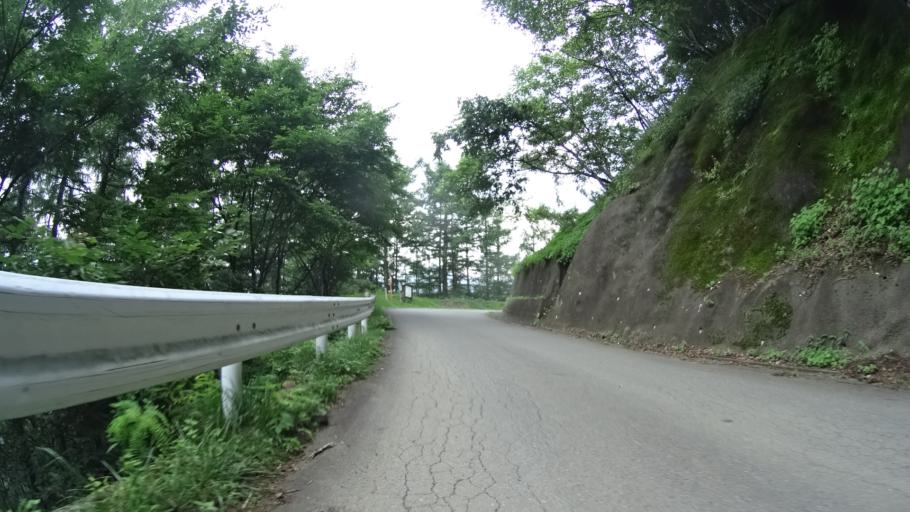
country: JP
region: Nagano
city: Saku
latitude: 36.0966
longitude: 138.6786
